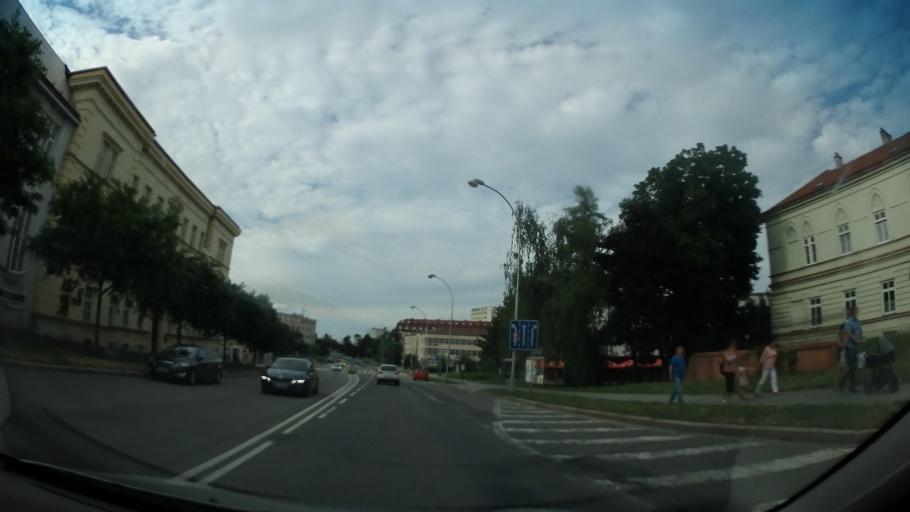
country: CZ
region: Zlin
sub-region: Okres Kromeriz
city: Kromeriz
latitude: 49.2977
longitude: 17.3983
